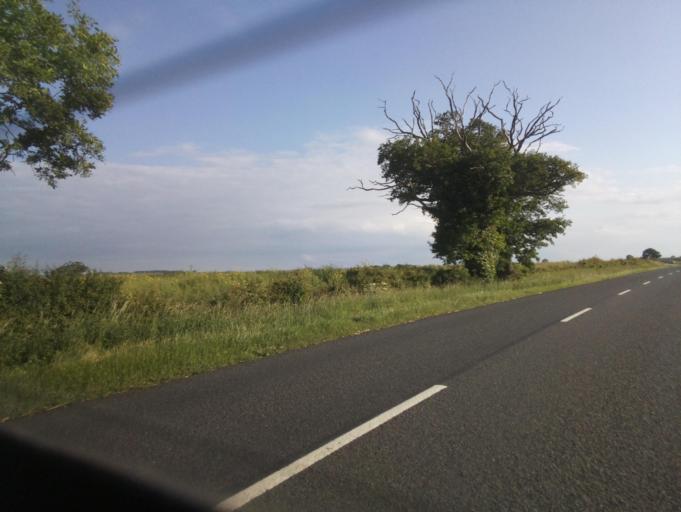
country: GB
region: England
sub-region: Lincolnshire
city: Navenby
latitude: 53.1104
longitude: -0.6008
